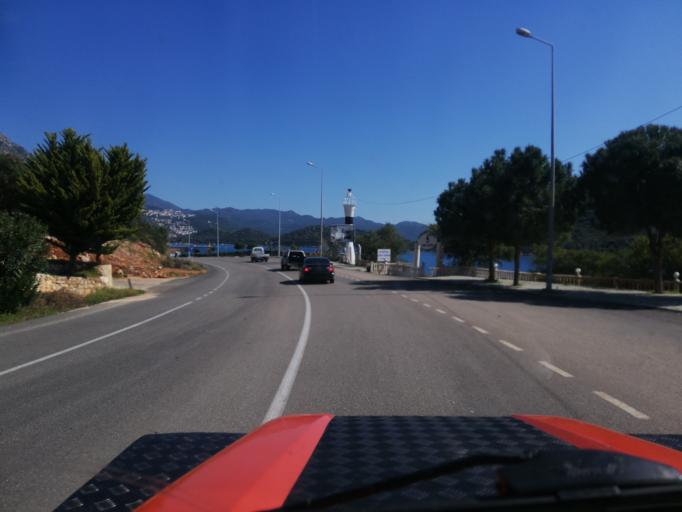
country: TR
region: Antalya
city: Kas
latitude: 36.2079
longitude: 29.6151
